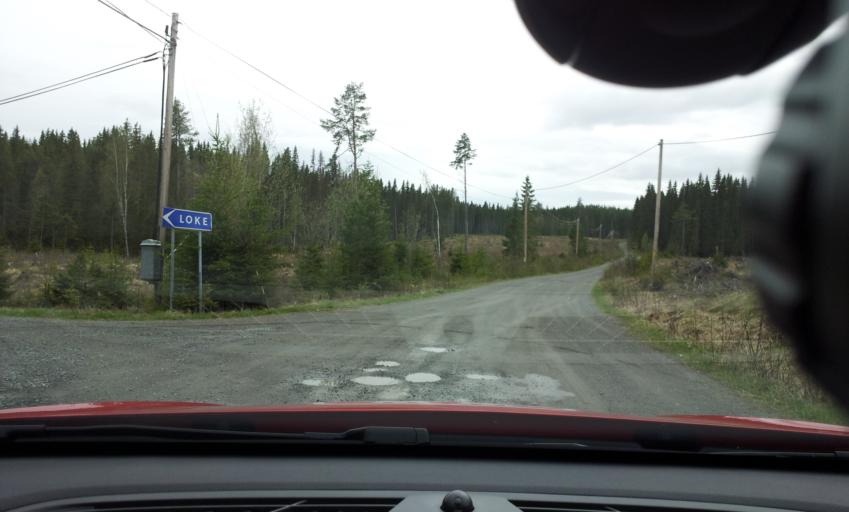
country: SE
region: Jaemtland
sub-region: OEstersunds Kommun
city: Brunflo
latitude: 63.0178
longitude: 14.7705
